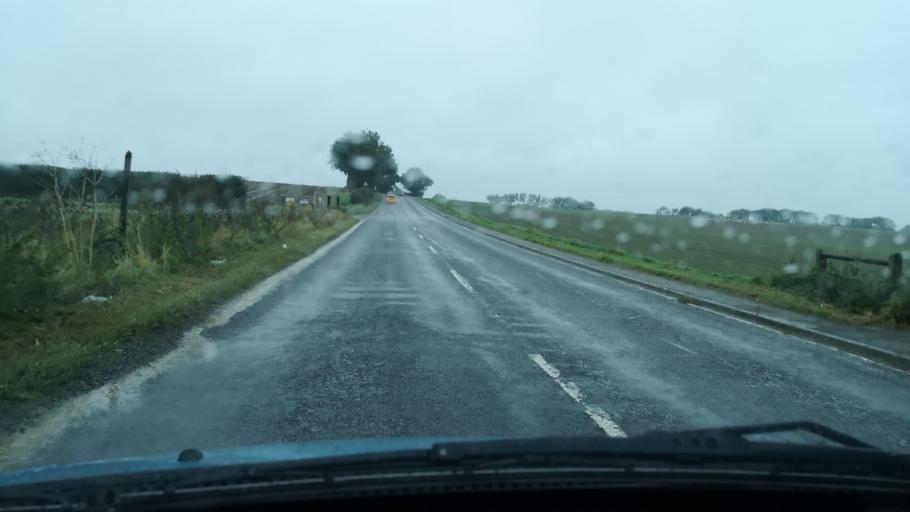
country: GB
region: England
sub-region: City and Borough of Wakefield
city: Low Ackworth
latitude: 53.6341
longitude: -1.3352
